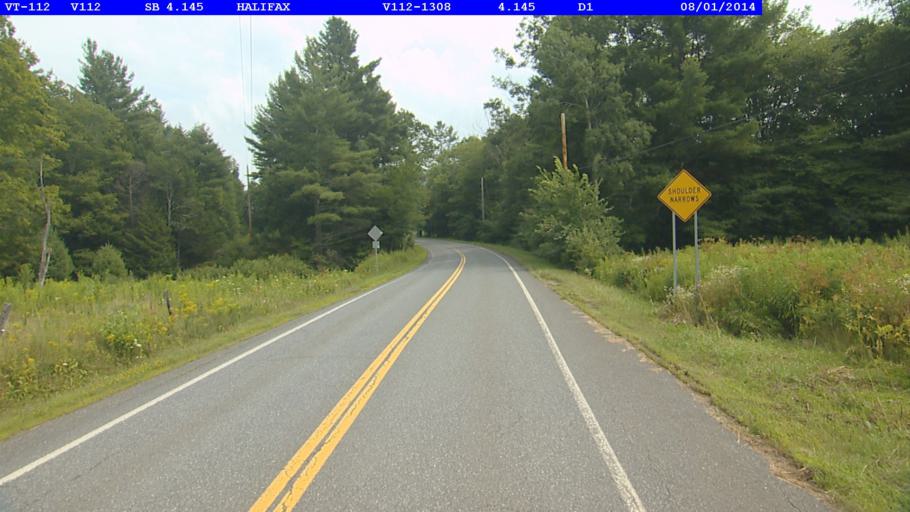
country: US
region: Massachusetts
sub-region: Franklin County
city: Colrain
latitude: 42.7635
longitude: -72.7837
